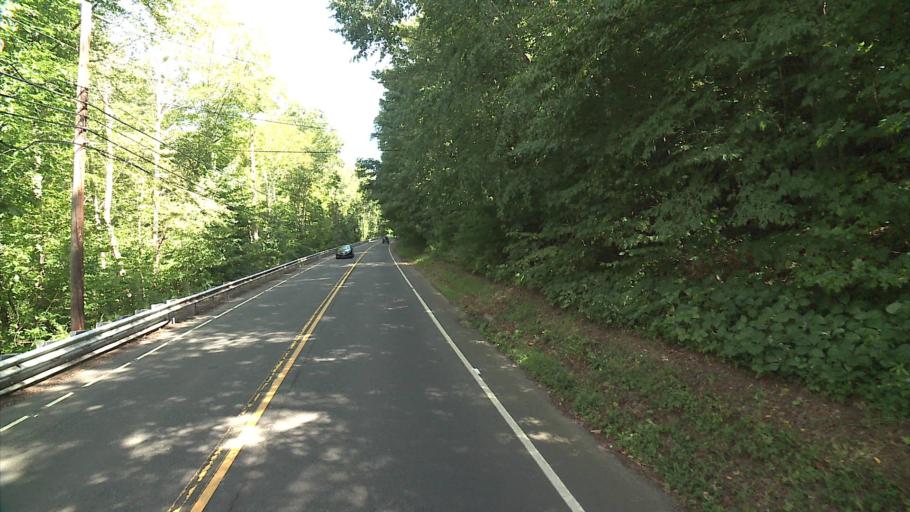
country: US
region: Connecticut
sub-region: New Haven County
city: Meriden
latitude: 41.5288
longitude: -72.8491
